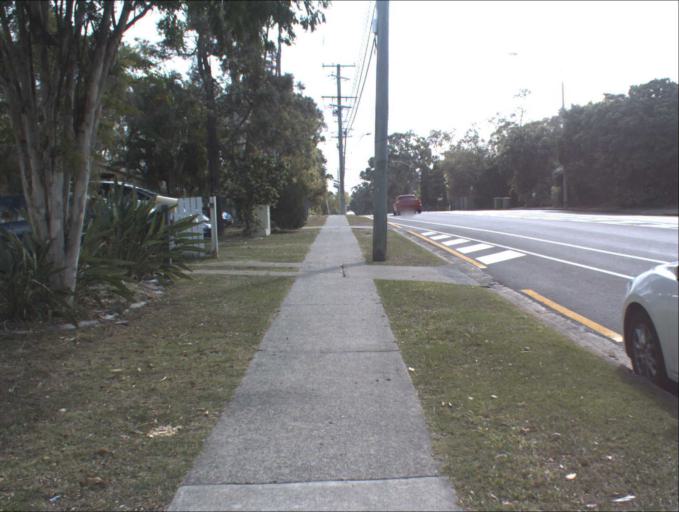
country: AU
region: Queensland
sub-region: Logan
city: Waterford West
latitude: -27.6703
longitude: 153.1328
